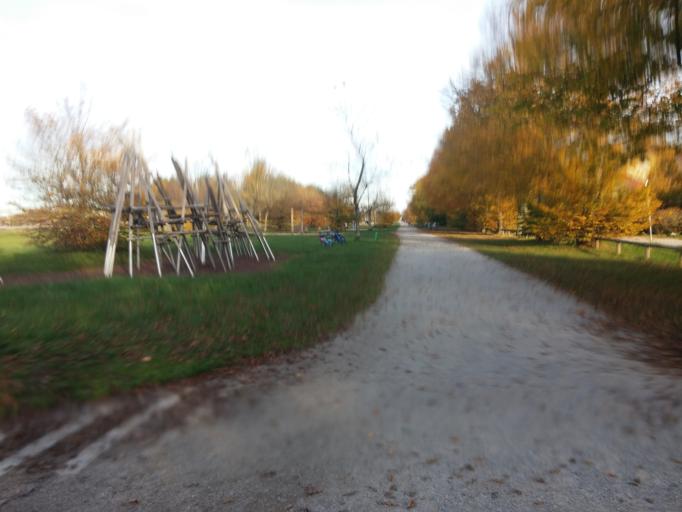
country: DE
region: Bavaria
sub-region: Upper Bavaria
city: Haar
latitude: 48.1246
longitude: 11.6971
